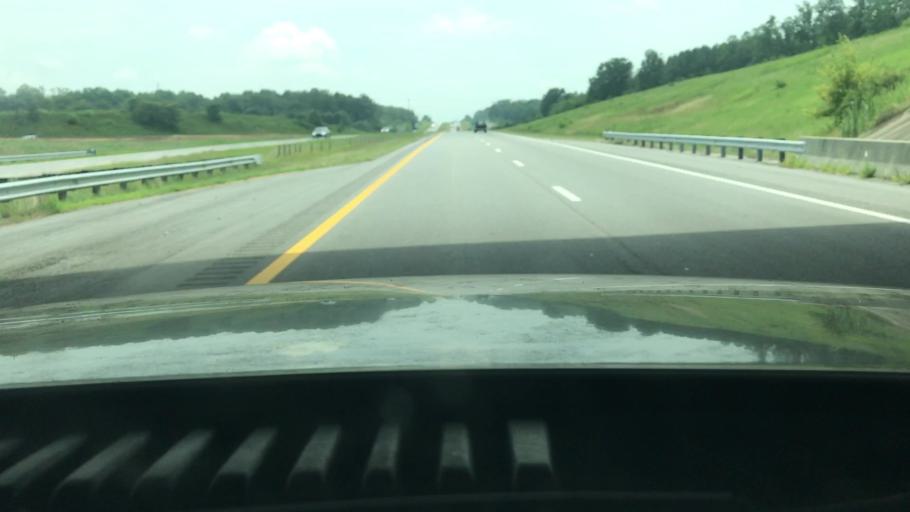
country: US
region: North Carolina
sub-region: Yadkin County
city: Jonesville
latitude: 36.1305
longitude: -80.8423
